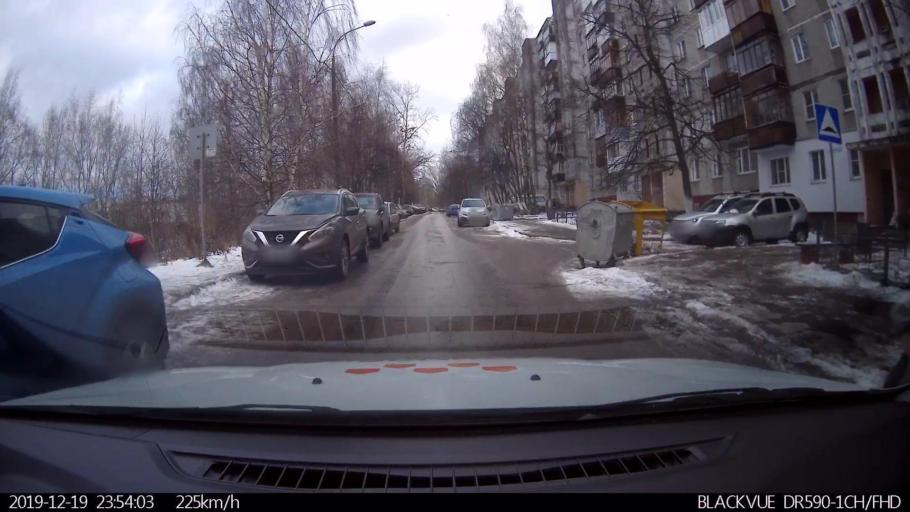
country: RU
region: Vologda
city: Molochnoye
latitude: 58.9475
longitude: 39.5069
